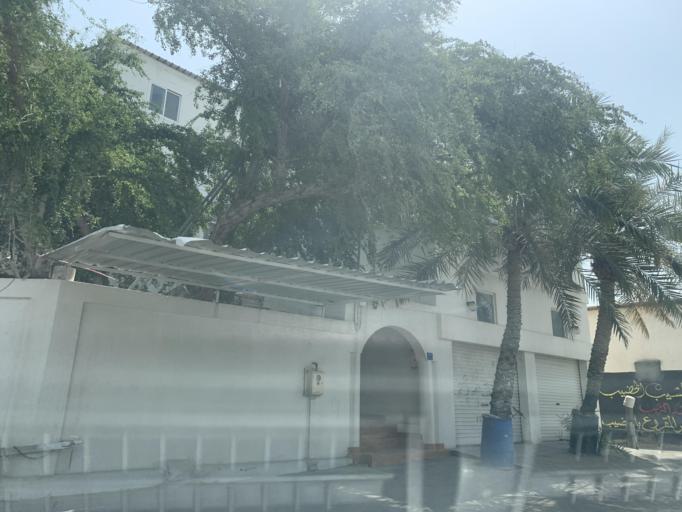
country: BH
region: Northern
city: Madinat `Isa
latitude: 26.1851
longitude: 50.5499
